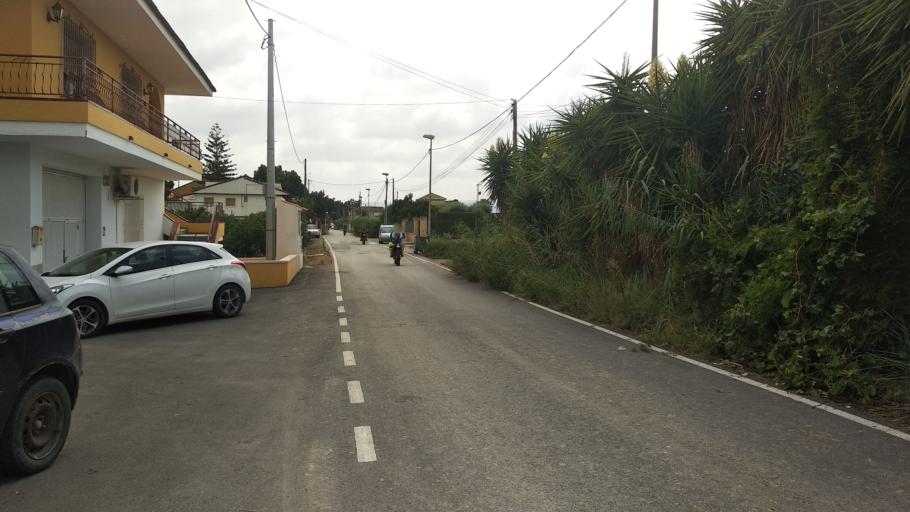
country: ES
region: Murcia
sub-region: Murcia
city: Santomera
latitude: 38.0411
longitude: -1.0342
